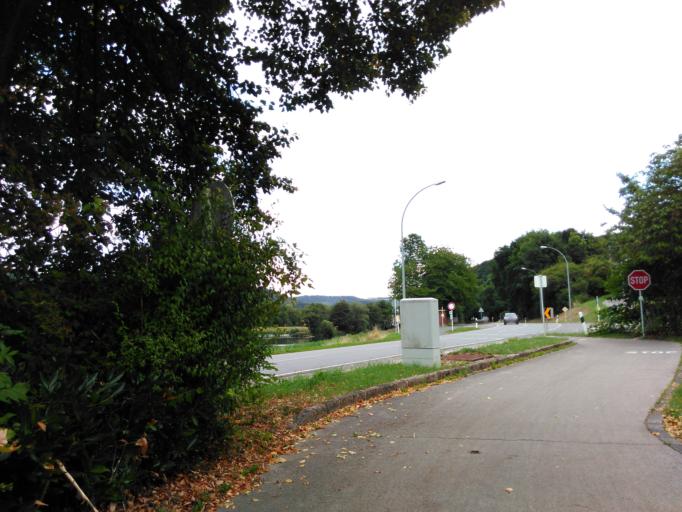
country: DE
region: Rheinland-Pfalz
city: Menningen
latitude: 49.8146
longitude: 6.4811
